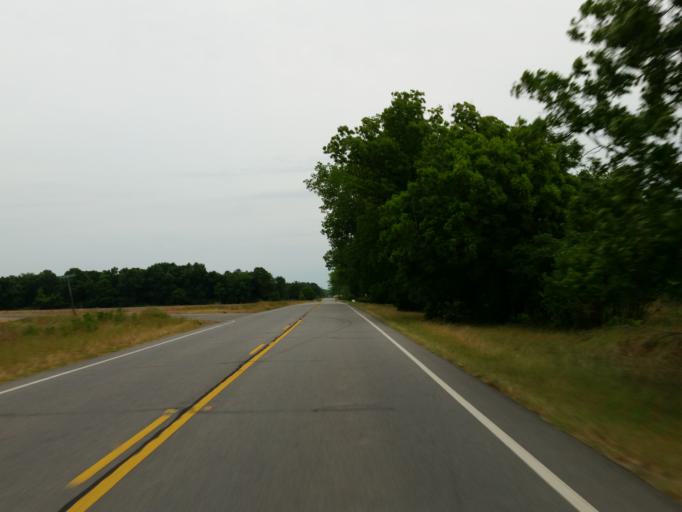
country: US
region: Georgia
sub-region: Dooly County
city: Unadilla
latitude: 32.2134
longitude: -83.7594
